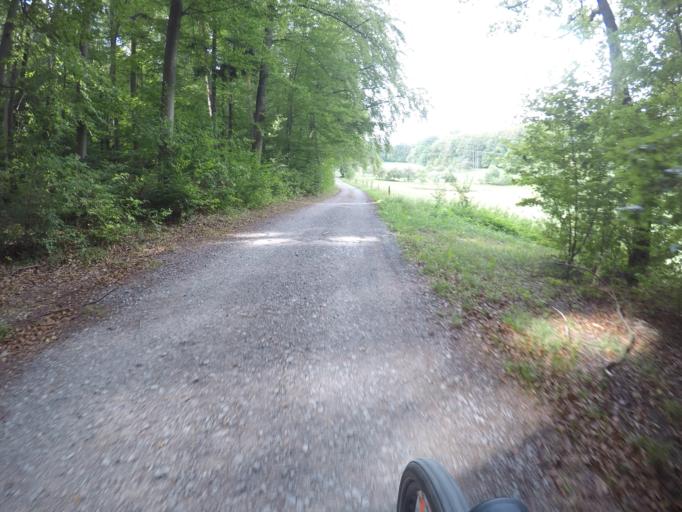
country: DE
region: Baden-Wuerttemberg
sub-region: Karlsruhe Region
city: Simmozheim
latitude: 48.7381
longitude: 8.8155
